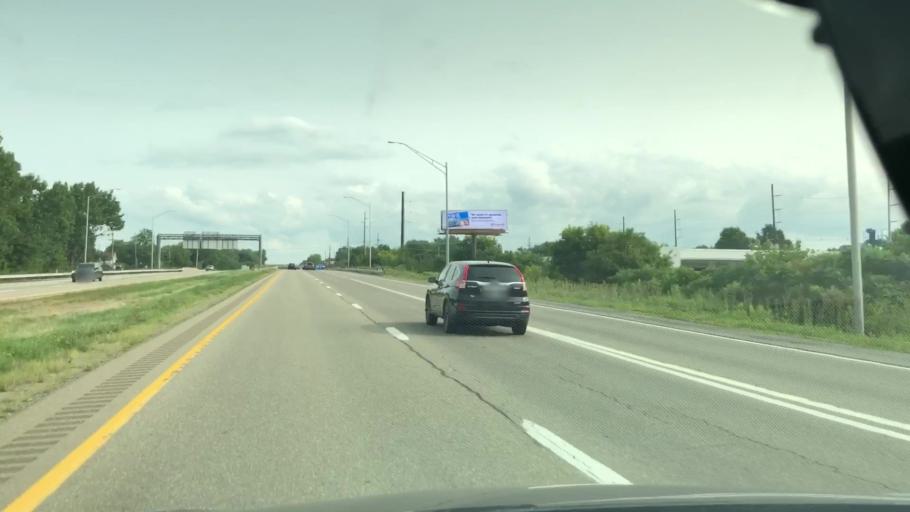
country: US
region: Pennsylvania
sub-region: Erie County
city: Erie
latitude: 42.0912
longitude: -80.1200
